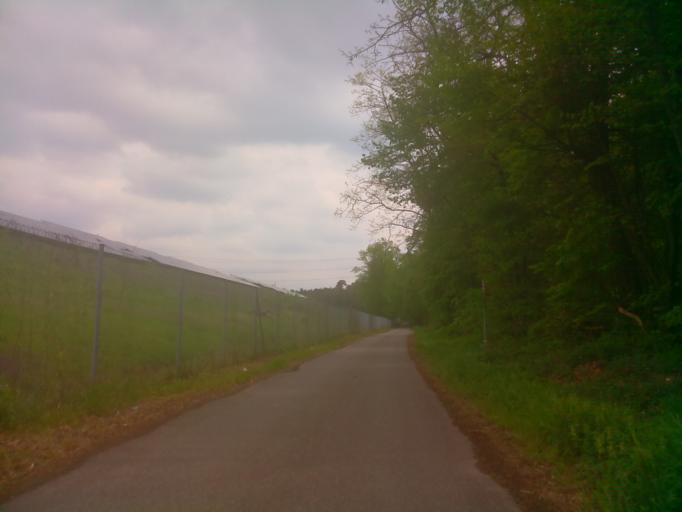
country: DE
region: Baden-Wuerttemberg
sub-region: Karlsruhe Region
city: Oftersheim
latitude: 49.3539
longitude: 8.6210
